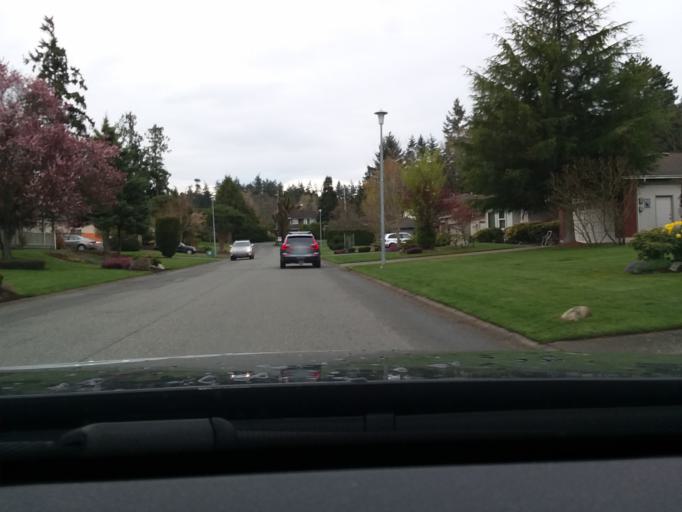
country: CA
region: British Columbia
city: Victoria
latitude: 48.5154
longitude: -123.3785
